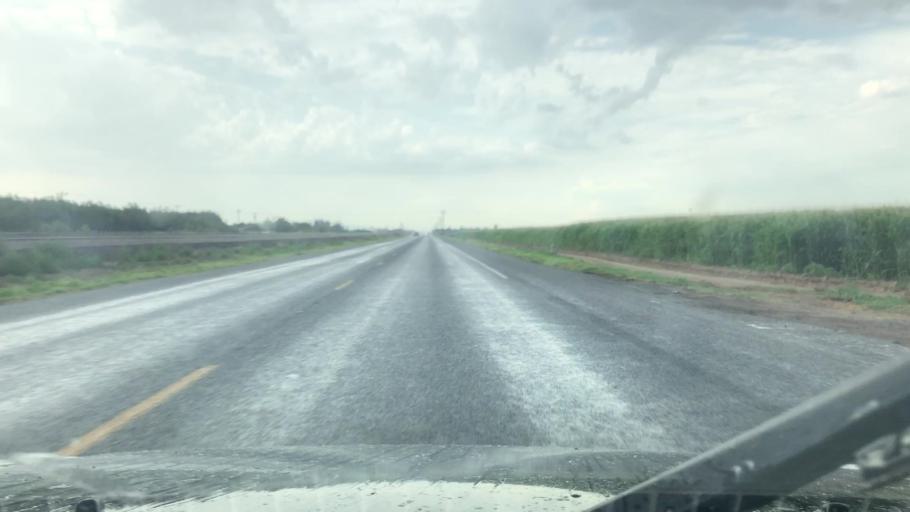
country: US
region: New Mexico
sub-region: Dona Ana County
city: Mesquite
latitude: 32.1498
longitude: -106.6872
